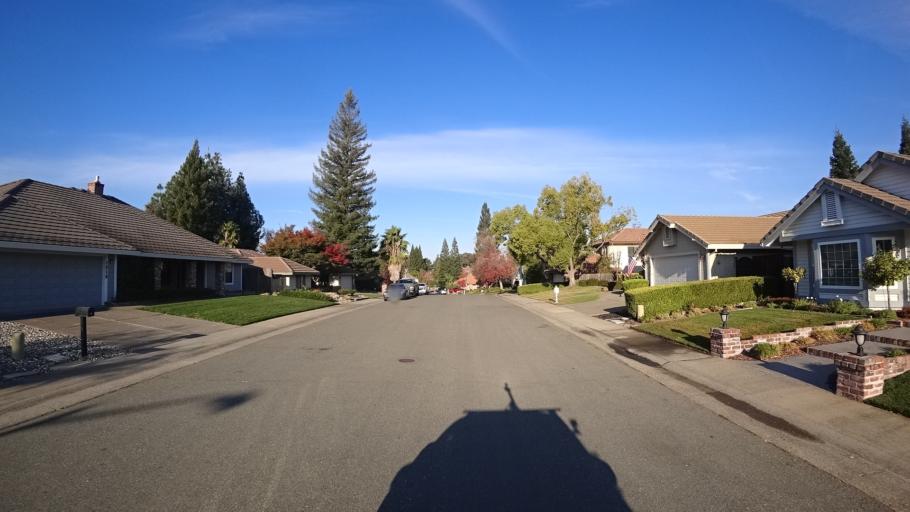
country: US
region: California
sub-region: Sacramento County
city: Citrus Heights
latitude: 38.7238
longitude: -121.2743
